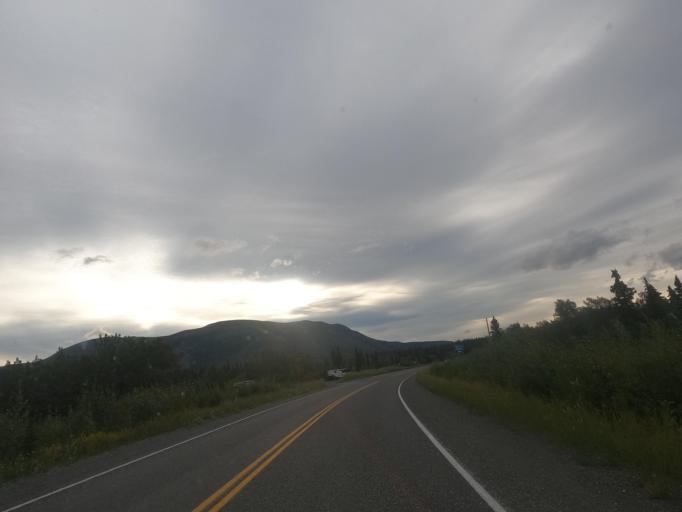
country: CA
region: Yukon
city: Haines Junction
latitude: 60.8589
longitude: -137.0630
